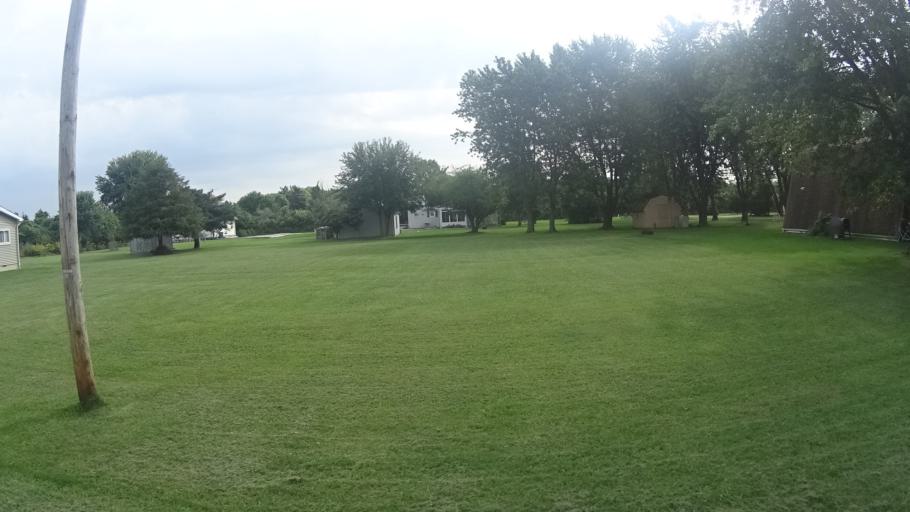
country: US
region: Ohio
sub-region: Erie County
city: Sandusky
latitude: 41.5894
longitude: -82.6898
